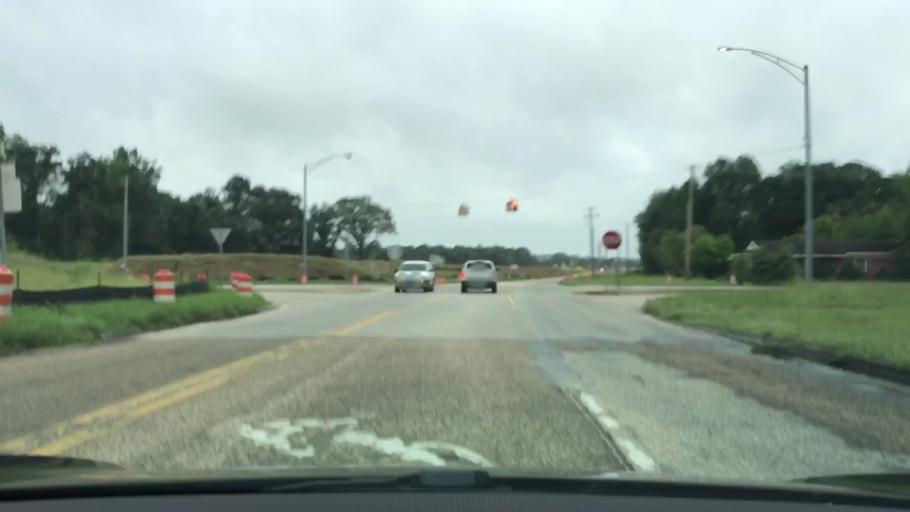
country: US
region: Alabama
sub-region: Coffee County
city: Elba
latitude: 31.4261
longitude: -86.0688
